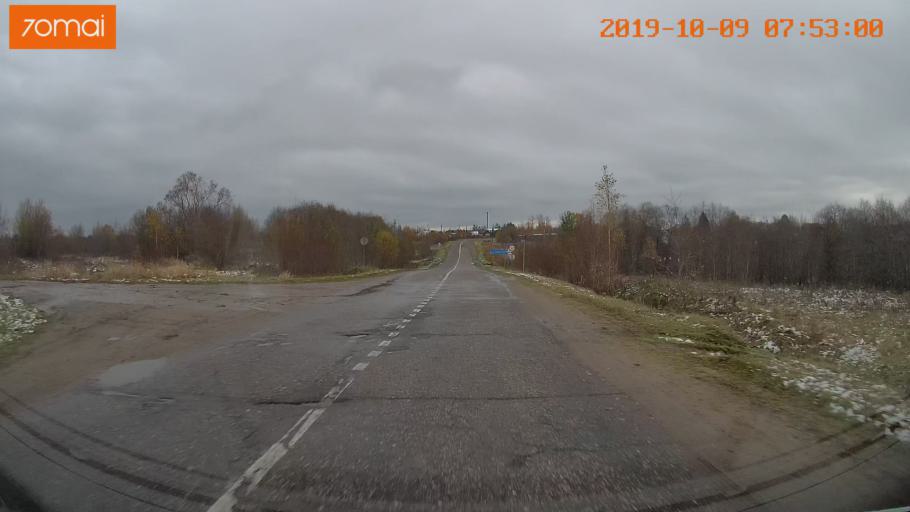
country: RU
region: Jaroslavl
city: Kukoboy
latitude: 58.6955
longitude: 39.8914
